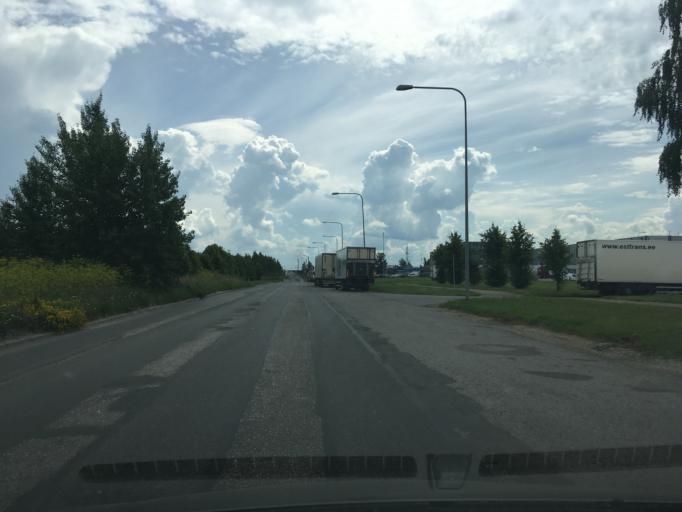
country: EE
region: Harju
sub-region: Tallinna linn
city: Kose
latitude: 59.4285
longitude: 24.8493
